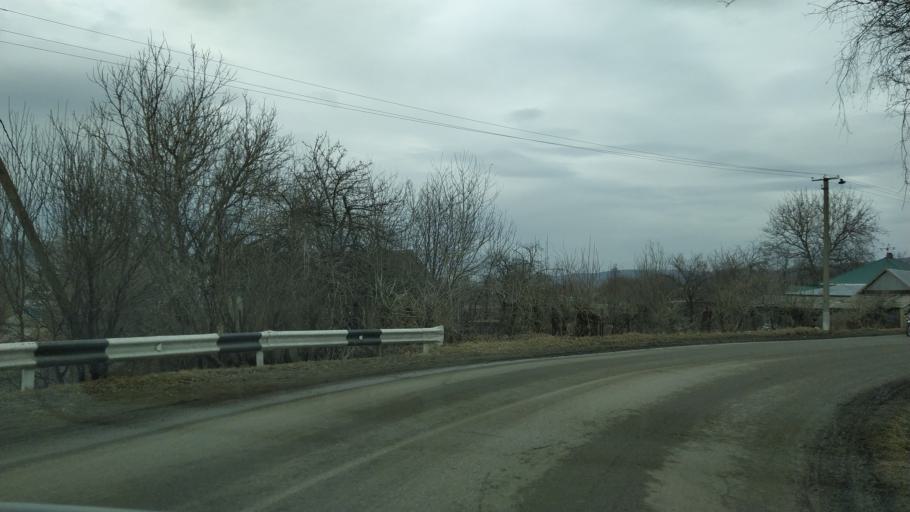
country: RU
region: Krasnodarskiy
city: Peredovaya
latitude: 44.1193
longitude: 41.4730
